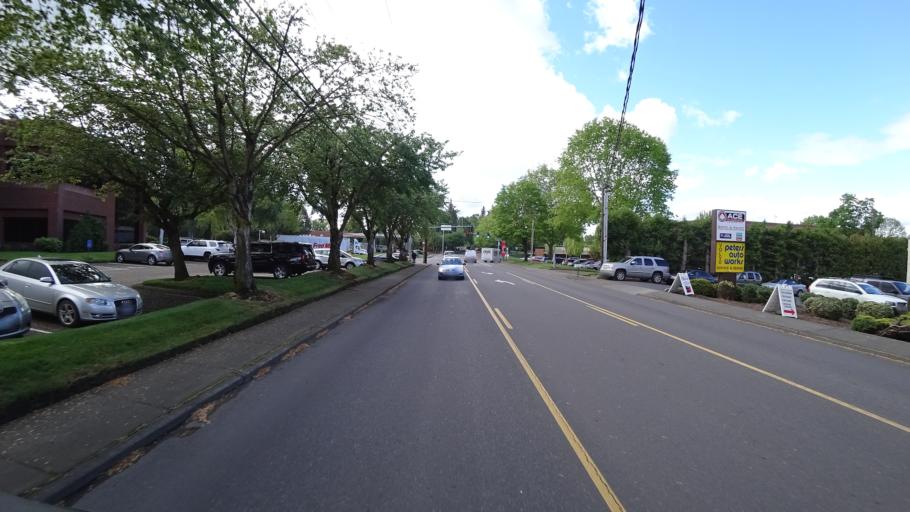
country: US
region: Oregon
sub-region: Washington County
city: Durham
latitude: 45.4059
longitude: -122.7490
